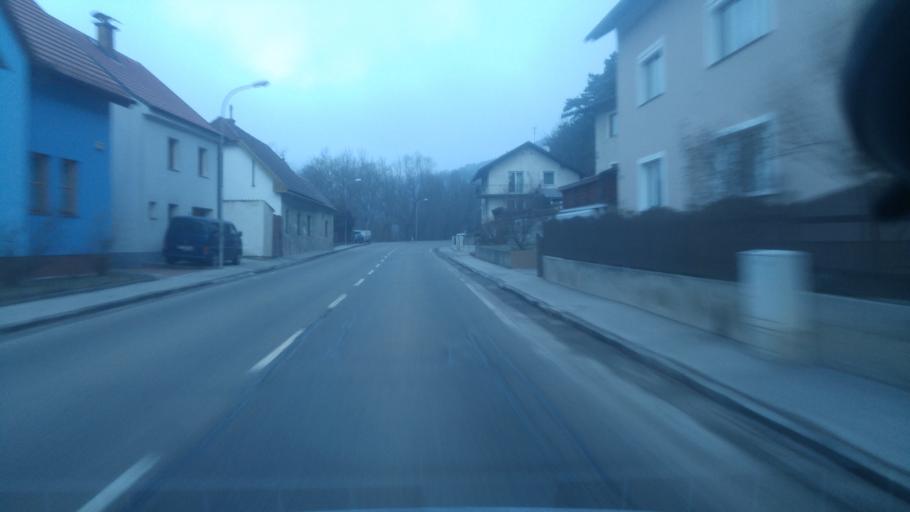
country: AT
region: Lower Austria
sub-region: Politischer Bezirk Baden
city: Pottenstein
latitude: 47.9752
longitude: 16.0704
